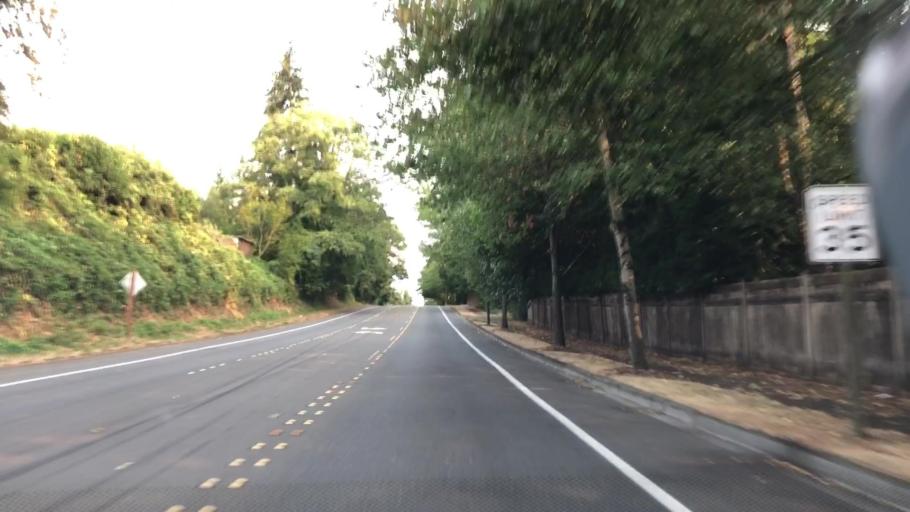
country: US
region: Washington
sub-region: King County
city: Mercer Island
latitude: 47.5667
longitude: -122.2265
